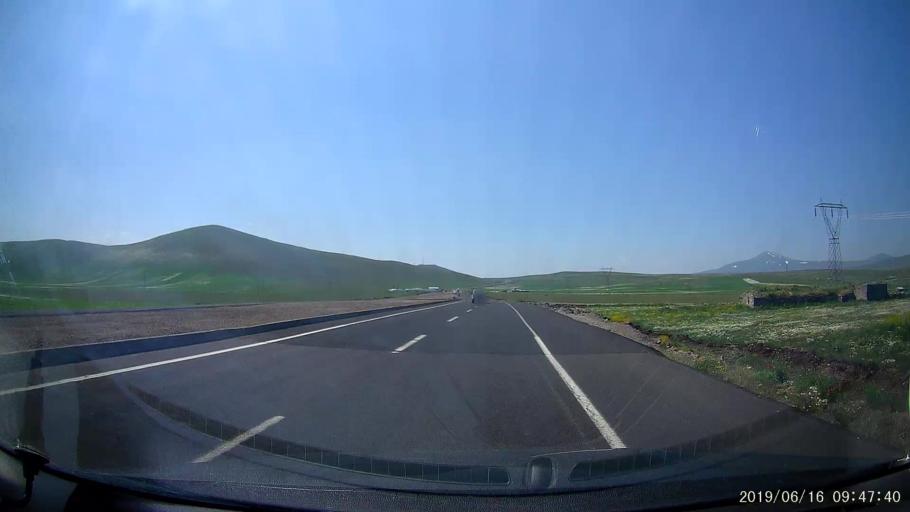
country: TR
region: Kars
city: Digor
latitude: 40.4432
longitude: 43.3465
